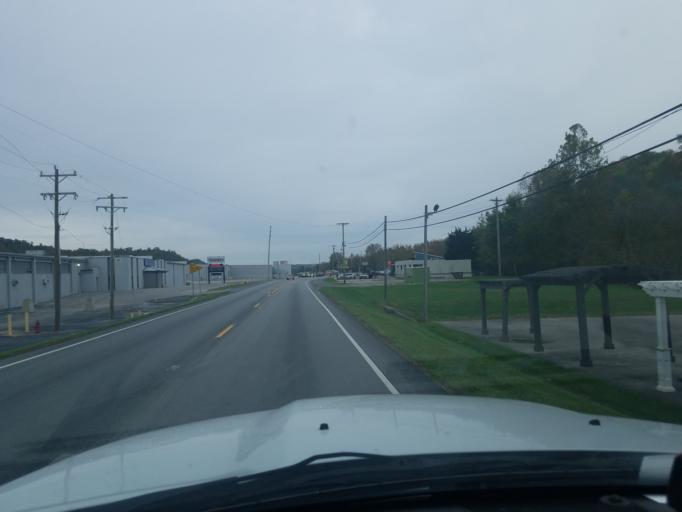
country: US
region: Indiana
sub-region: Washington County
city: New Pekin
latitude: 38.4651
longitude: -85.9421
